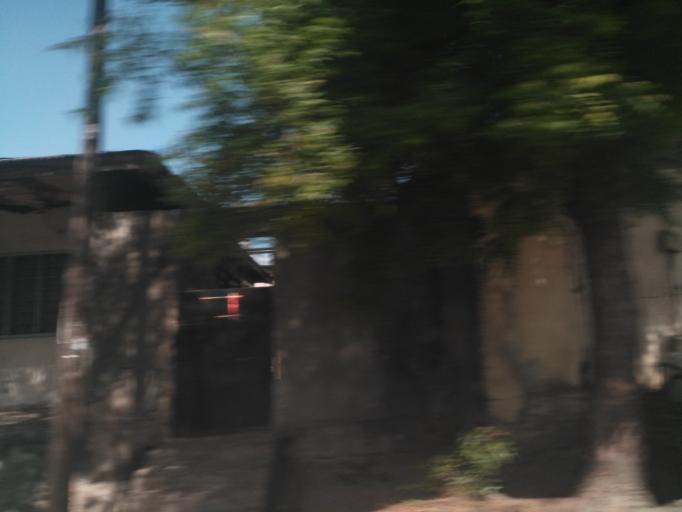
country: TZ
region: Dar es Salaam
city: Dar es Salaam
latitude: -6.8671
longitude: 39.2560
